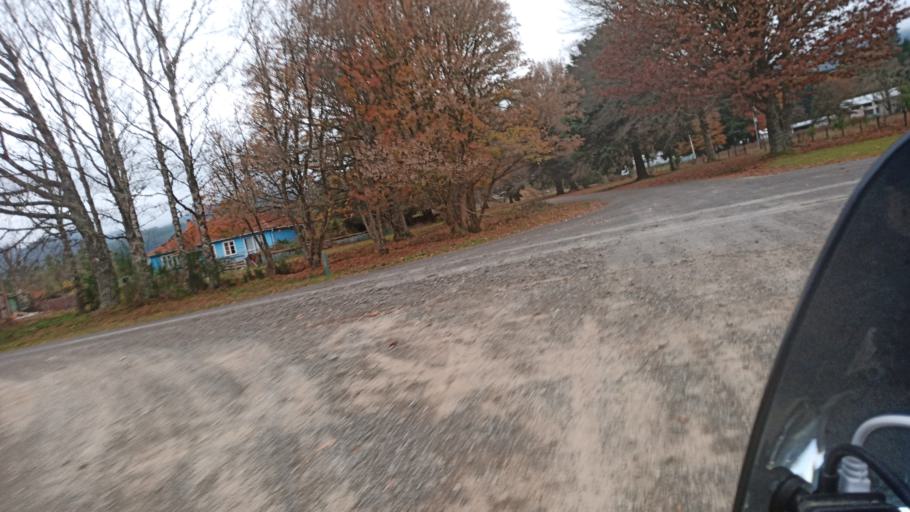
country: NZ
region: Bay of Plenty
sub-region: Whakatane District
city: Murupara
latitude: -38.6401
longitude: 176.7265
